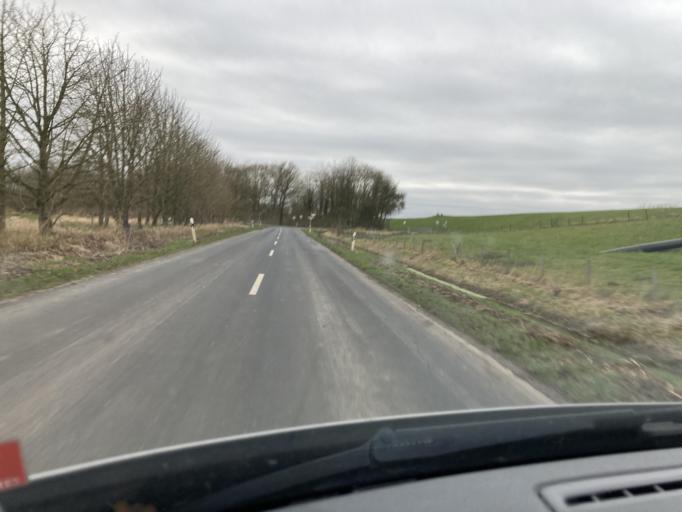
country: DE
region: Lower Saxony
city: Leer
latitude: 53.2063
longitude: 7.4225
